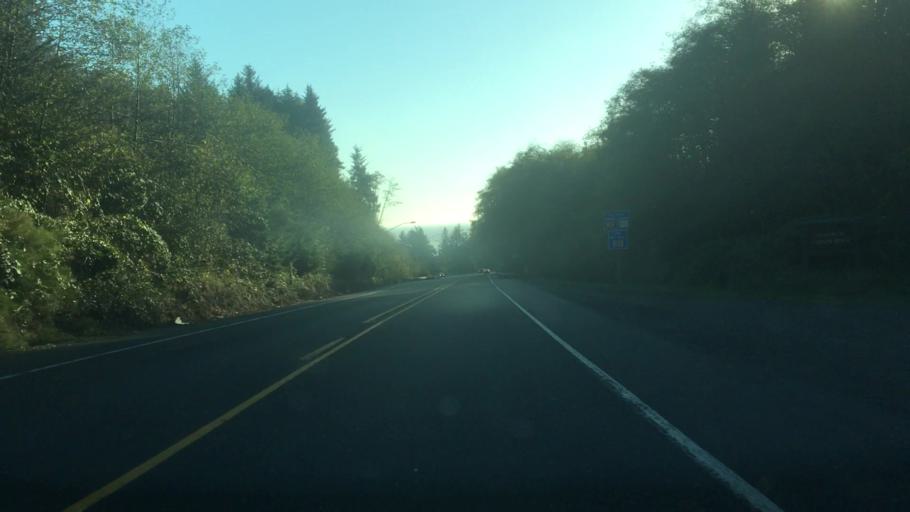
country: US
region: Oregon
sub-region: Clatsop County
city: Cannon Beach
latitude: 45.9095
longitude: -123.9504
